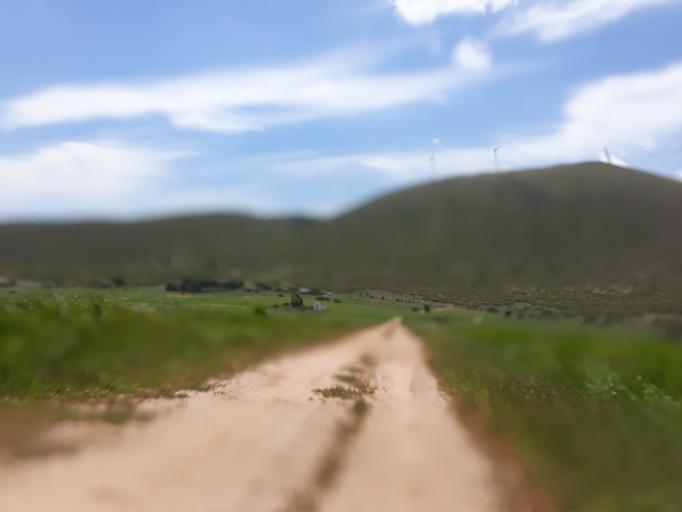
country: GR
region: Central Greece
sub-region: Nomos Voiotias
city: Ayios Thomas
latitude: 38.1863
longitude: 23.5613
